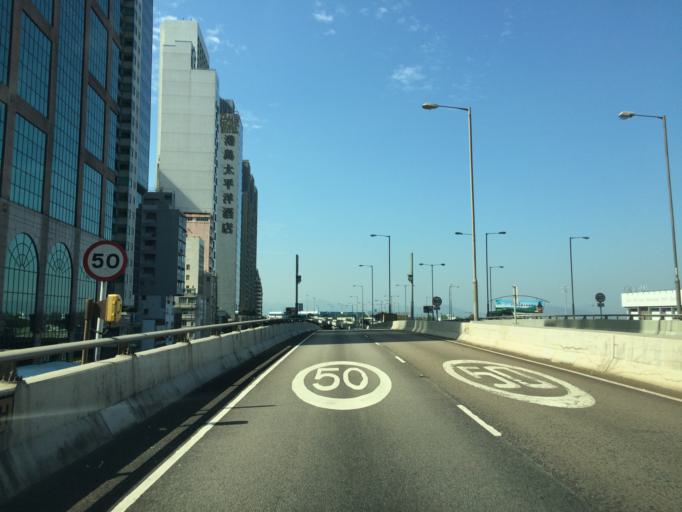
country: HK
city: Hong Kong
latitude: 22.2886
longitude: 114.1454
